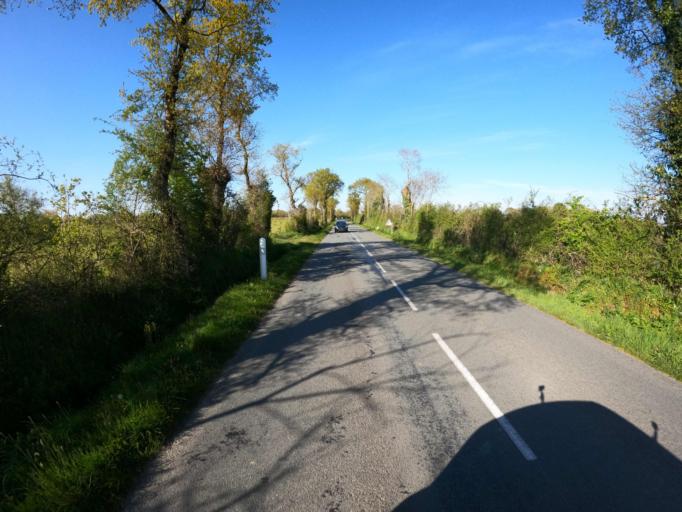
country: FR
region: Pays de la Loire
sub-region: Departement de la Vendee
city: Beaurepaire
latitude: 46.9253
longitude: -1.1157
